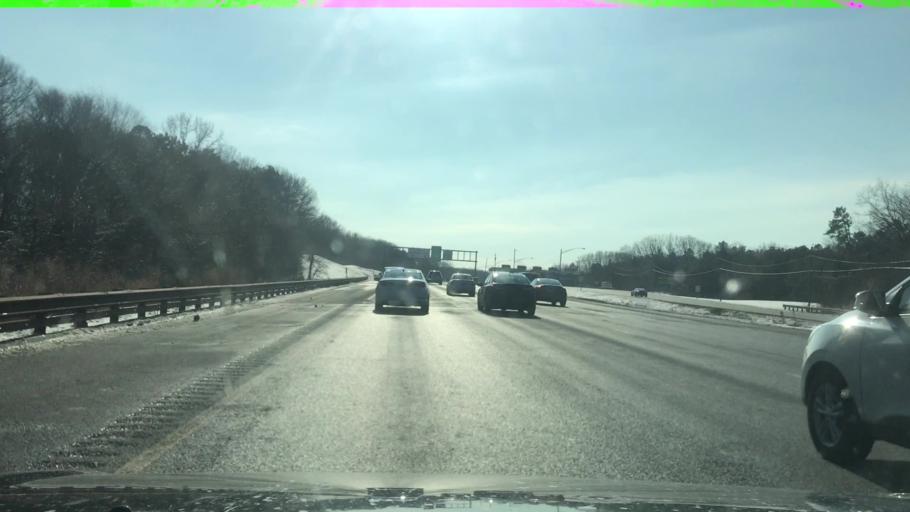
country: US
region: New Jersey
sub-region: Monmouth County
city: Shark River Hills
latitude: 40.1771
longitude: -74.1007
